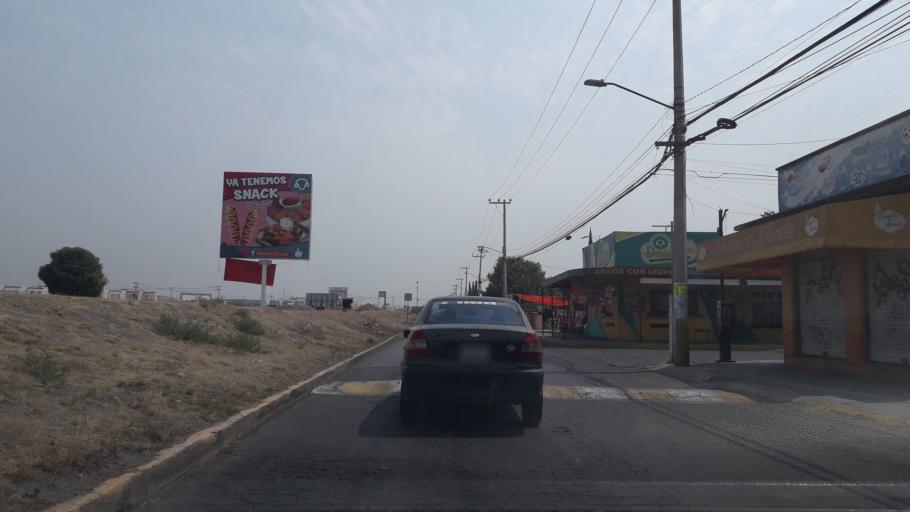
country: MX
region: Mexico
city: Ecatepec
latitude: 19.6222
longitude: -99.0367
